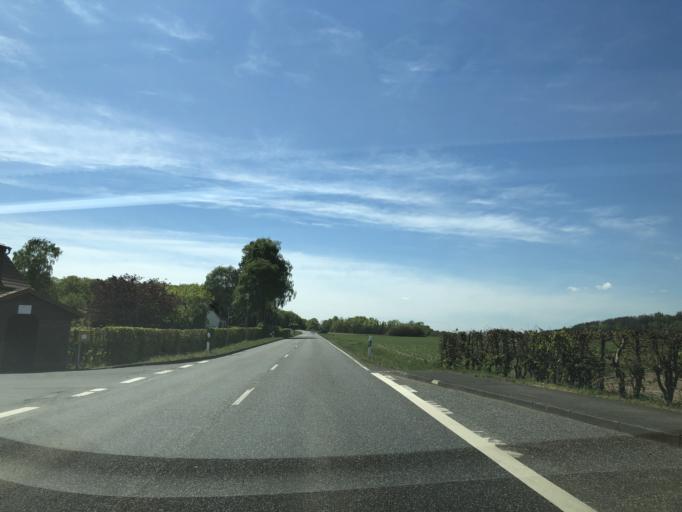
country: DE
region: Hesse
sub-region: Regierungsbezirk Kassel
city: Homberg
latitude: 51.0618
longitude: 9.4440
